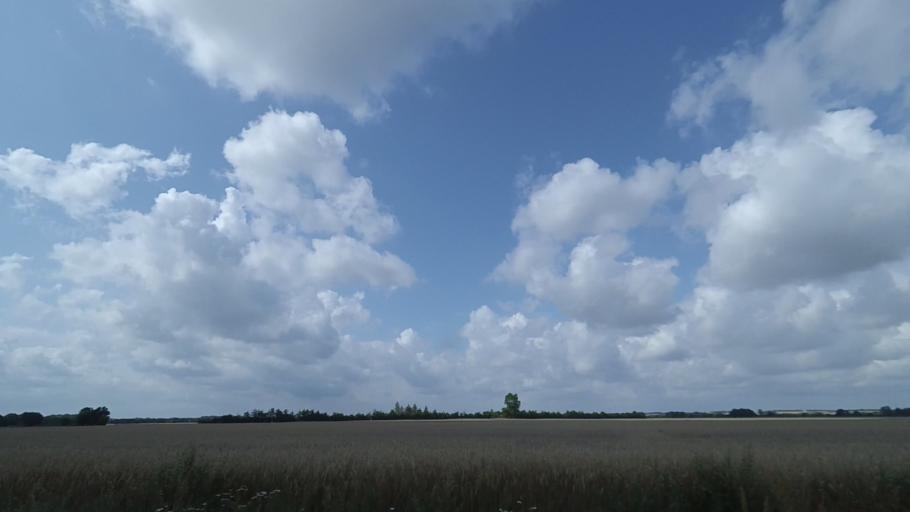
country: DK
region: Central Jutland
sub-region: Norddjurs Kommune
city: Auning
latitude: 56.5050
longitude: 10.4236
